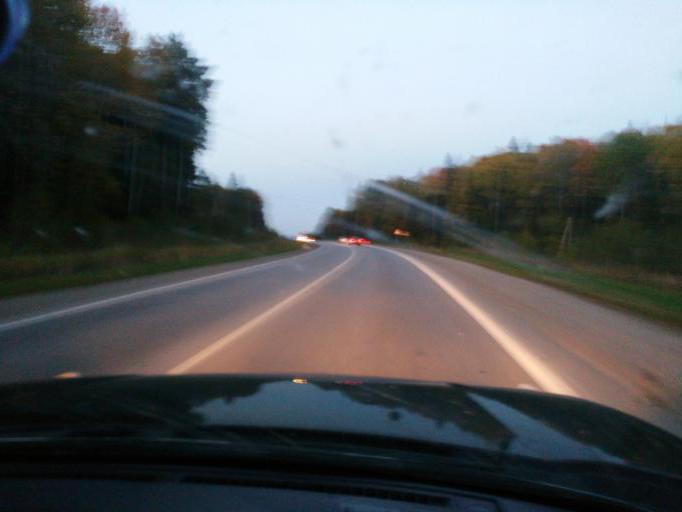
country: RU
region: Perm
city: Kalino
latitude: 58.2689
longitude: 57.3643
